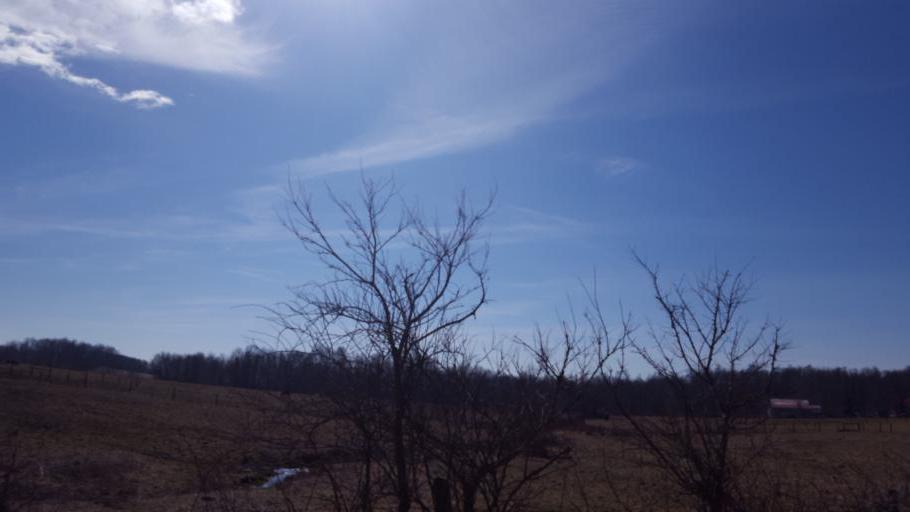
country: US
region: Ohio
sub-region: Knox County
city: Gambier
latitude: 40.5188
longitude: -82.3884
